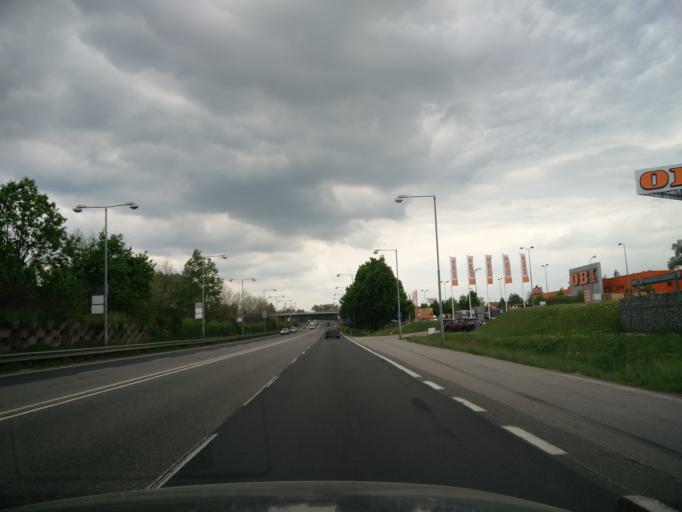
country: CZ
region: Jihocesky
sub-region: Okres Pisek
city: Pisek
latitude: 49.3008
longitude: 14.1405
